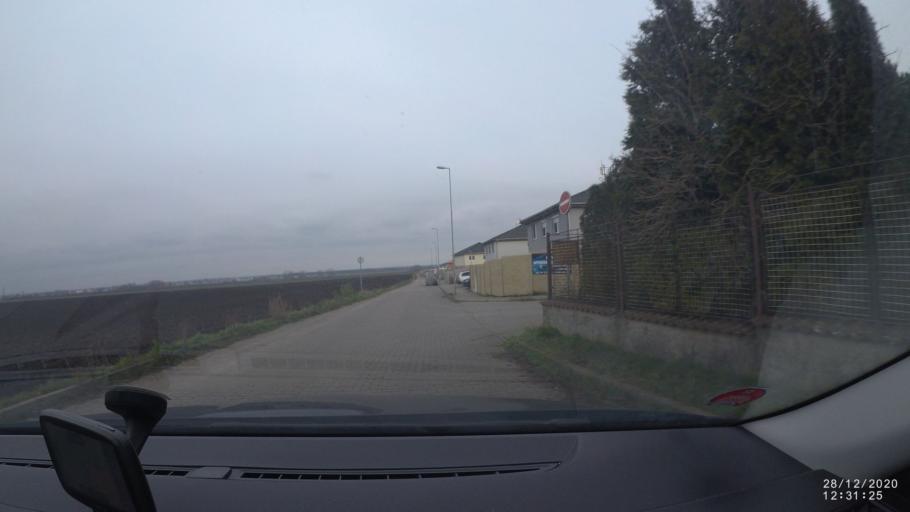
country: CZ
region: Central Bohemia
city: Kostelec nad Labem
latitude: 50.2023
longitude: 14.5898
